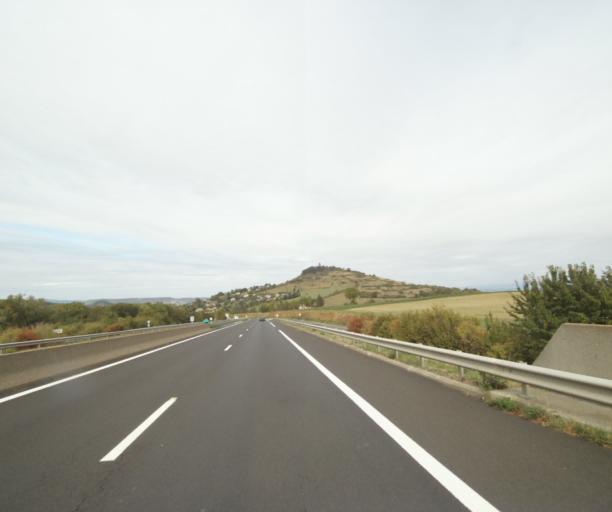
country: FR
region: Auvergne
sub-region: Departement du Puy-de-Dome
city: Ceyrat
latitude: 45.7197
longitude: 3.0705
